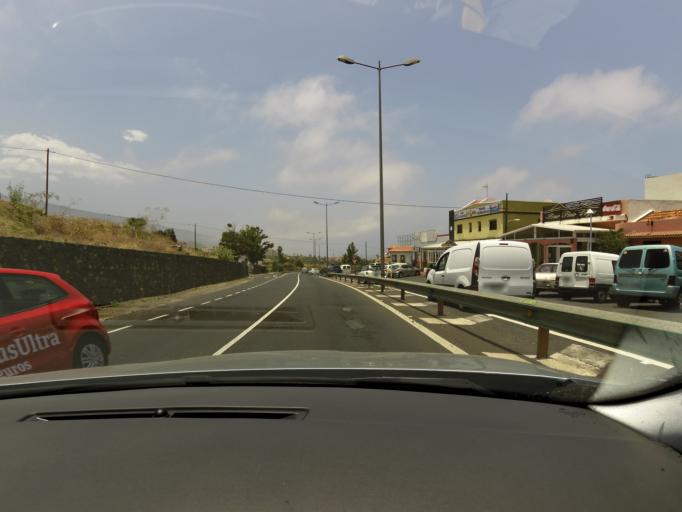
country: ES
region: Canary Islands
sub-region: Provincia de Santa Cruz de Tenerife
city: La Orotava
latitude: 28.4047
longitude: -16.5199
